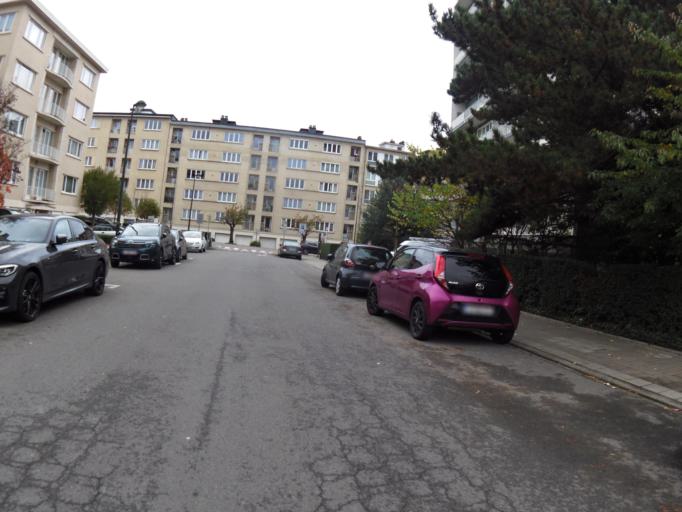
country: BE
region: Brussels Capital
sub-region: Bruxelles-Capitale
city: Brussels
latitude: 50.8227
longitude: 4.4100
